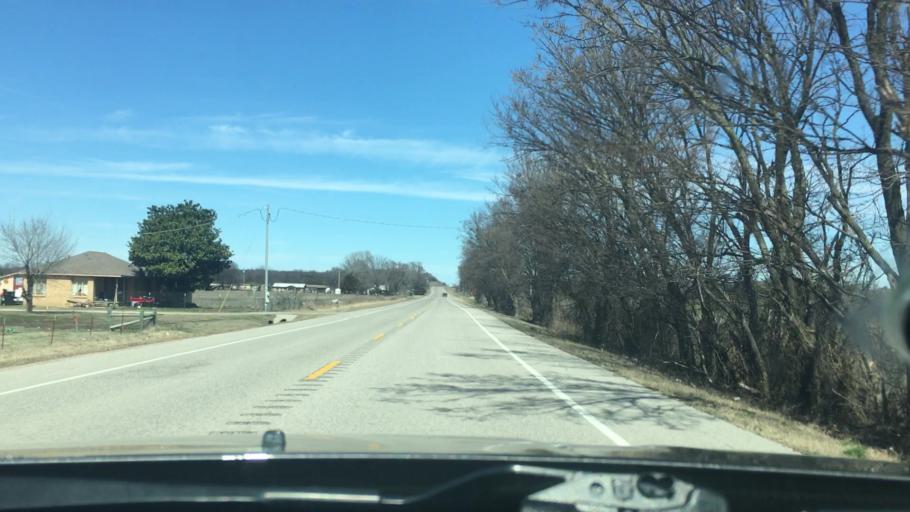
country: US
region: Oklahoma
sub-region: Murray County
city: Sulphur
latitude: 34.3942
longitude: -96.9511
